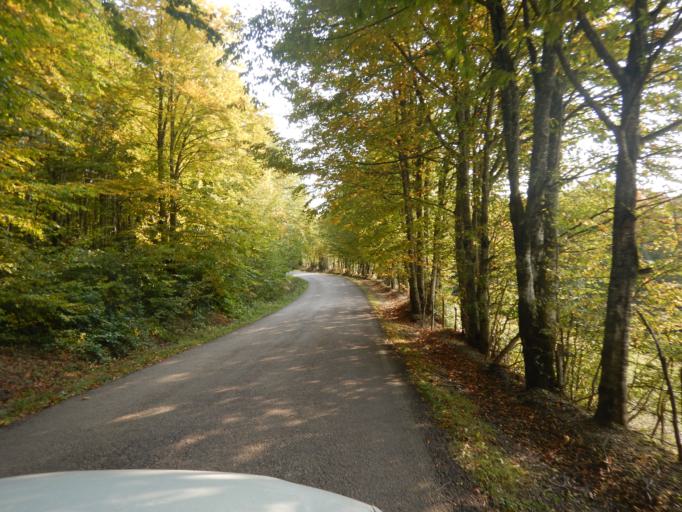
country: TR
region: Ordu
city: Golkoy
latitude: 40.6622
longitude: 37.5575
